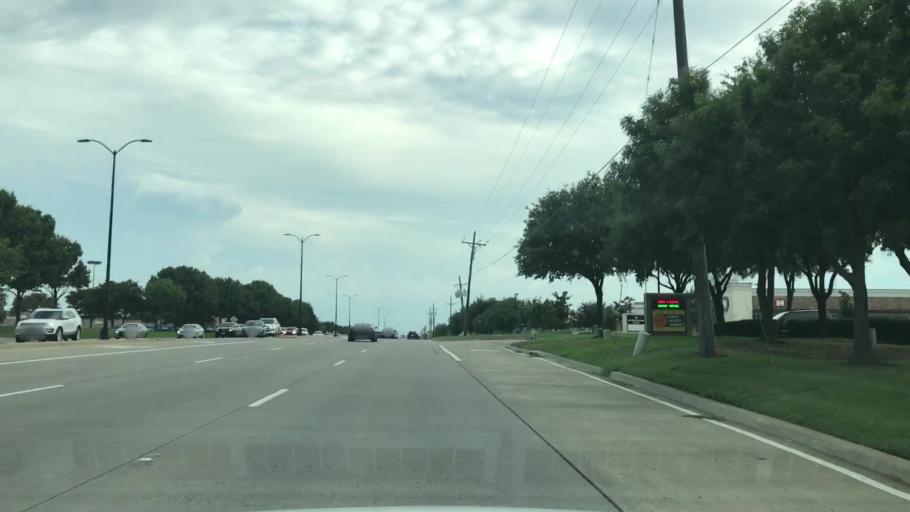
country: US
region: Texas
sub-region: Collin County
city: Frisco
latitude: 33.1200
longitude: -96.8057
